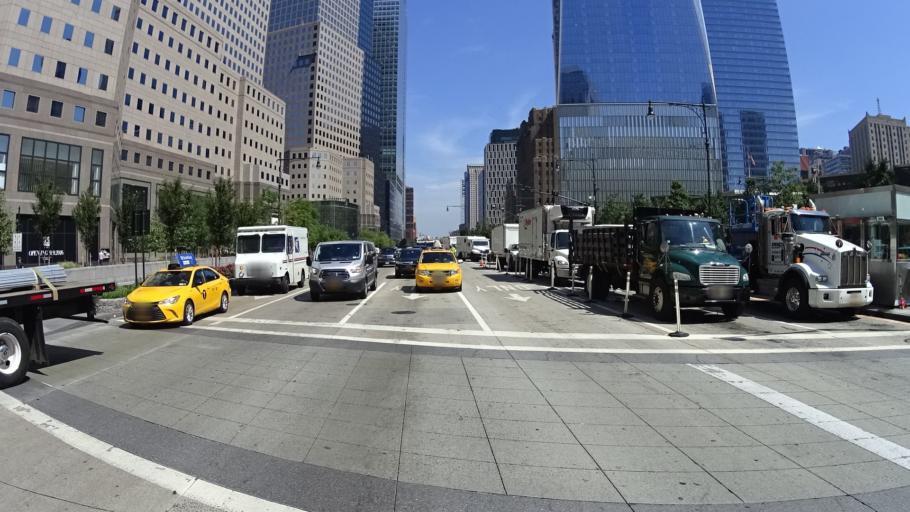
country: US
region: New York
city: New York City
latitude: 40.7112
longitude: -74.0147
